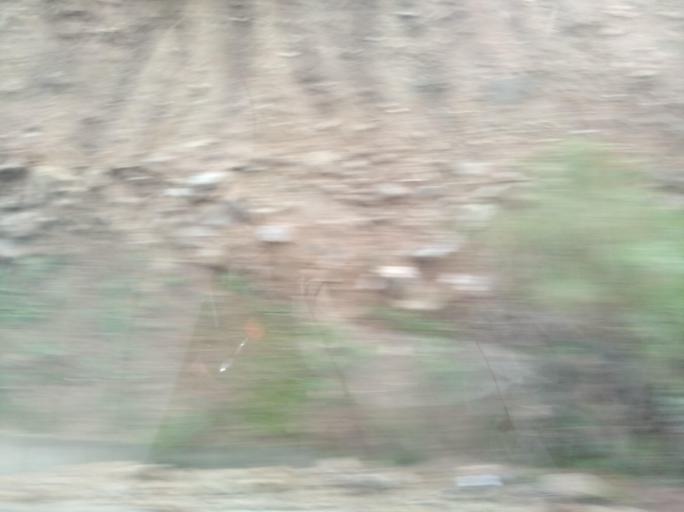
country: CL
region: Valparaiso
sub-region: Provincia de San Felipe
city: Llaillay
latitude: -33.0723
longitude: -70.9720
